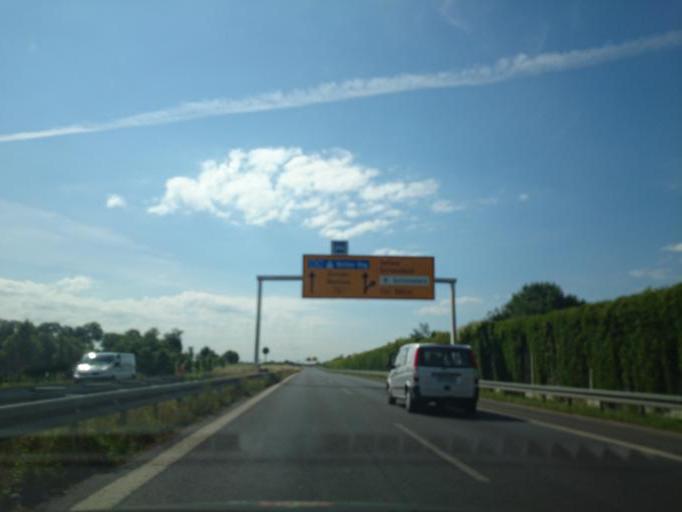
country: DE
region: Berlin
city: Lichtenrade
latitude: 52.3747
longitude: 13.4189
